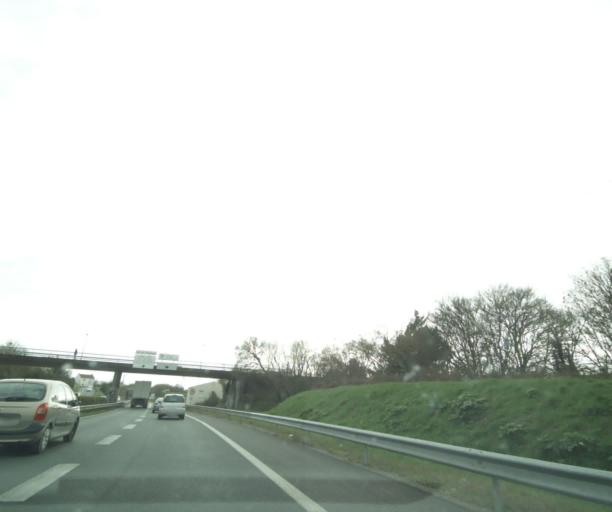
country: FR
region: Poitou-Charentes
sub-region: Departement de la Charente-Maritime
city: La Rochelle
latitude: 46.1675
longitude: -1.1921
